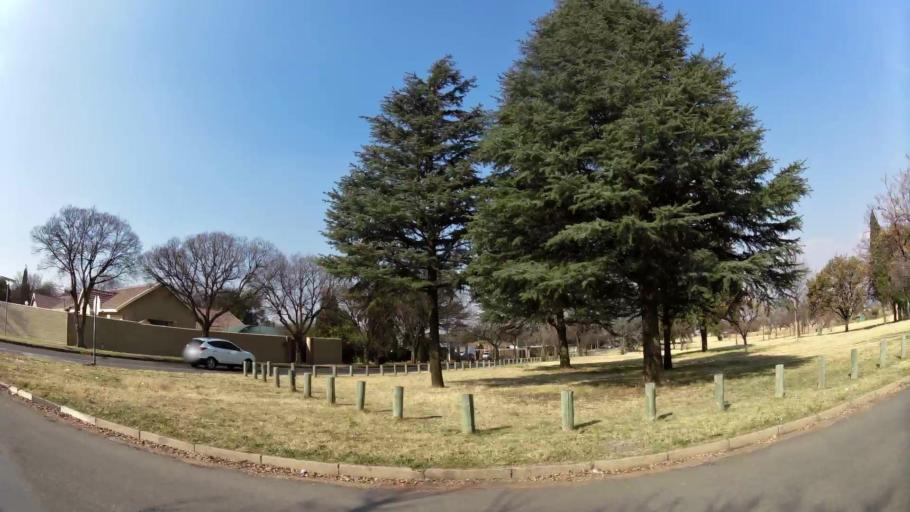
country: ZA
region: Gauteng
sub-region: Ekurhuleni Metropolitan Municipality
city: Boksburg
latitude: -26.1827
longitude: 28.2681
